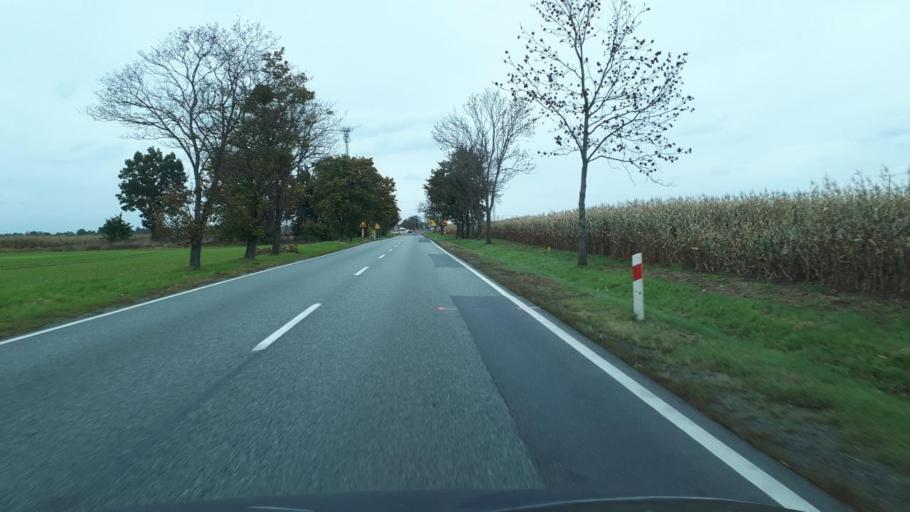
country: PL
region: Opole Voivodeship
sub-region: Powiat kluczborski
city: Byczyna
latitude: 51.0948
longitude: 18.2027
